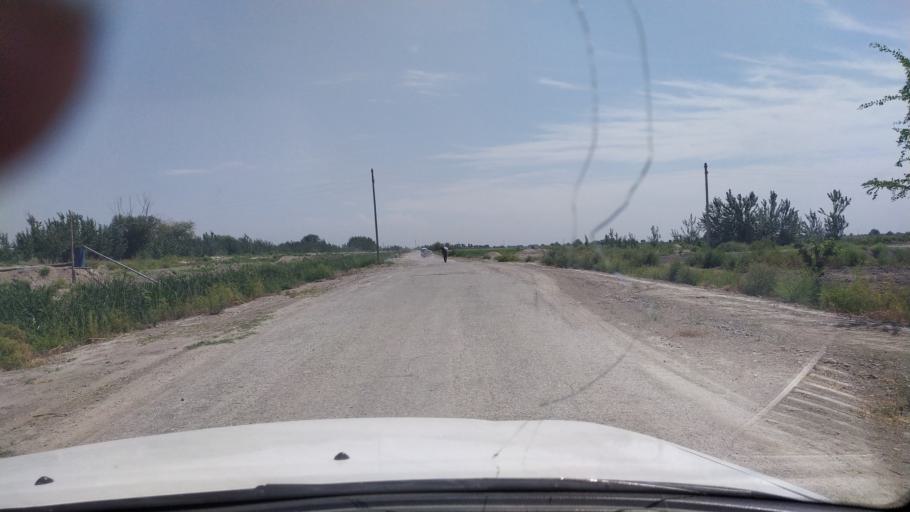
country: UZ
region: Namangan
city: Toshbuloq
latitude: 40.7954
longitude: 71.5823
